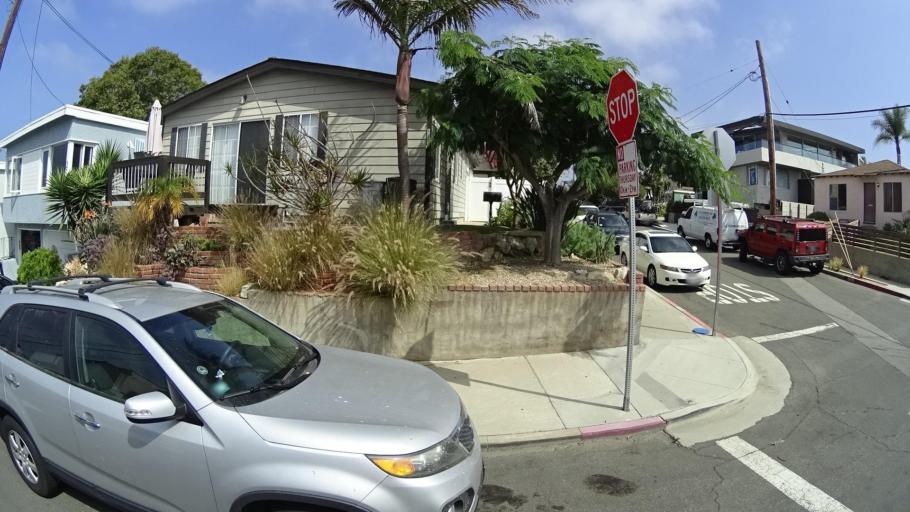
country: US
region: California
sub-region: Los Angeles County
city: Redondo Beach
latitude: 33.8575
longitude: -118.3888
